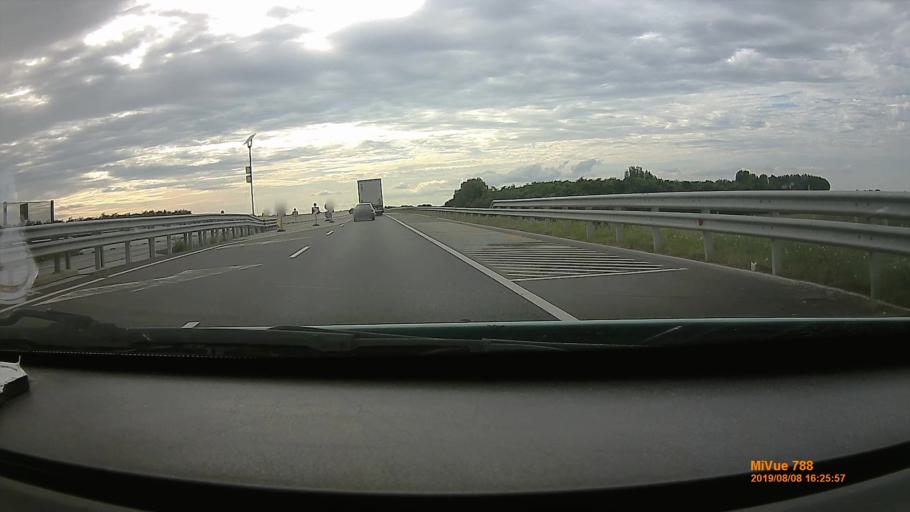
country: HU
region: Szabolcs-Szatmar-Bereg
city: Hodasz
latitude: 47.9709
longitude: 22.2078
